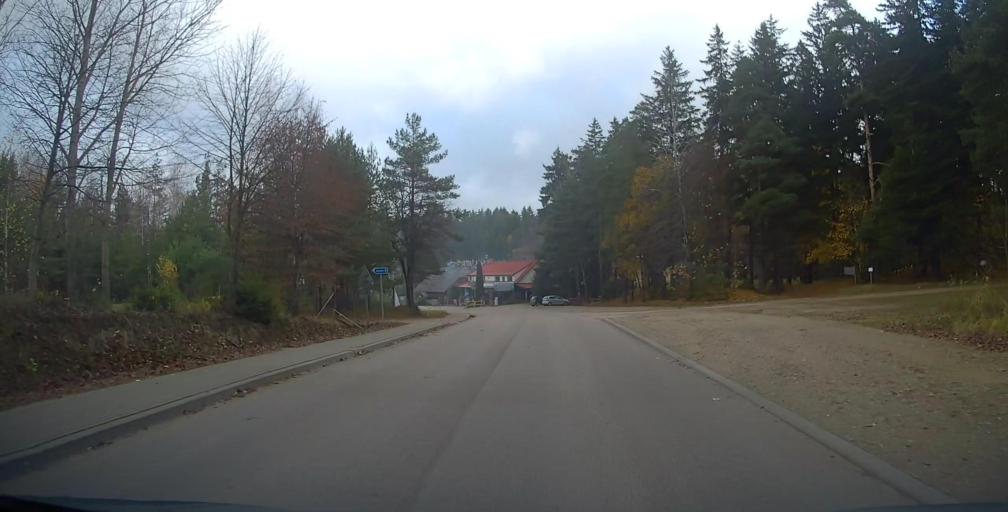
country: PL
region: Podlasie
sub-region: Suwalki
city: Suwalki
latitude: 54.2862
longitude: 22.8890
